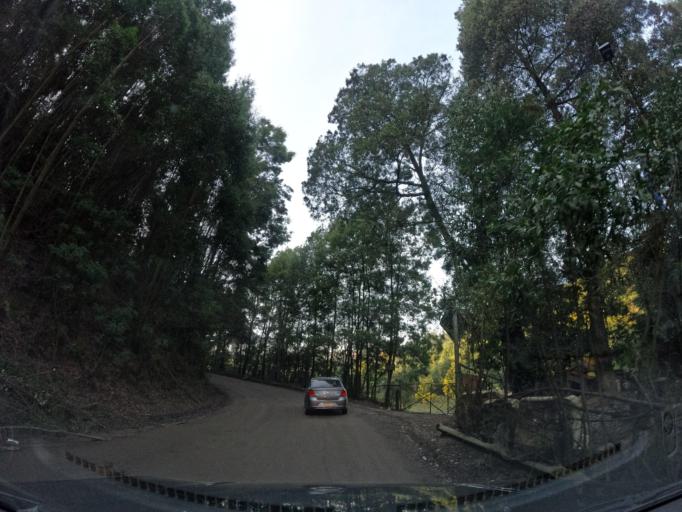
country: CL
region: Biobio
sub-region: Provincia de Concepcion
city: Concepcion
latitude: -36.8472
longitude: -73.0082
